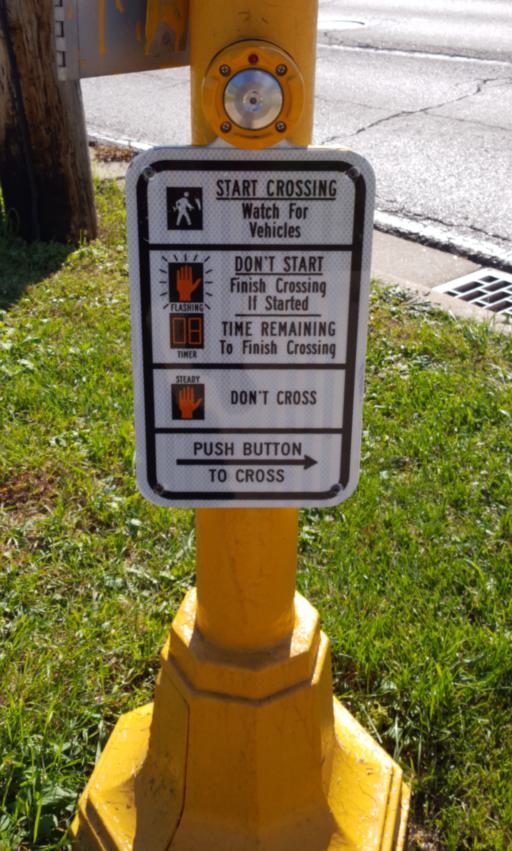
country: US
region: Illinois
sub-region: Cook County
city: Northfield
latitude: 42.0797
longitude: -87.7613
